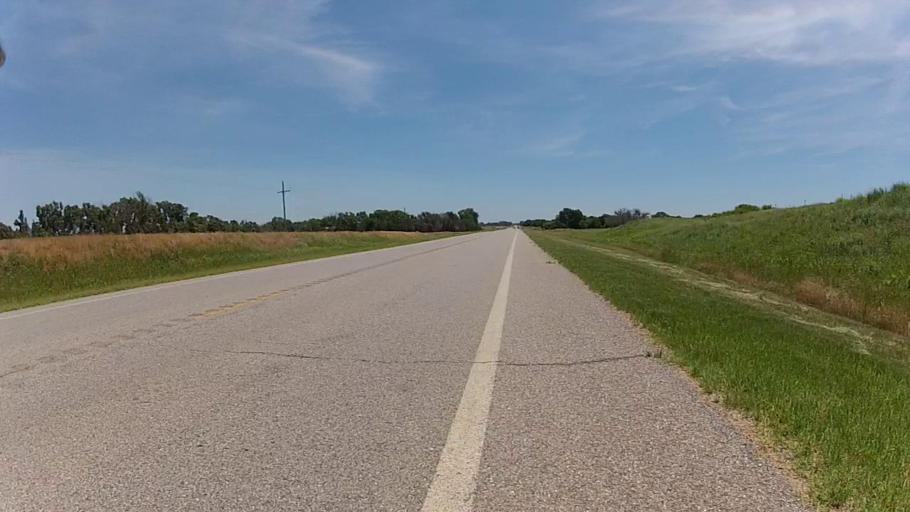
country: US
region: Kansas
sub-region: Barber County
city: Medicine Lodge
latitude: 37.2536
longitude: -98.4773
